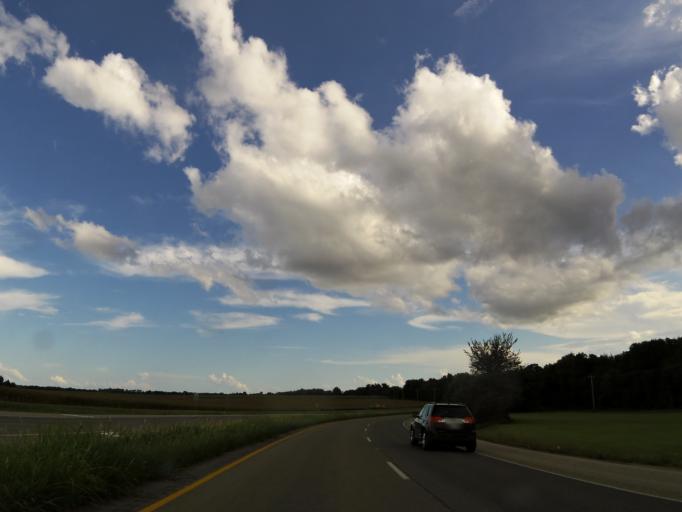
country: US
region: Kentucky
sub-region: Christian County
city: Hopkinsville
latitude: 36.7670
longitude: -87.4707
